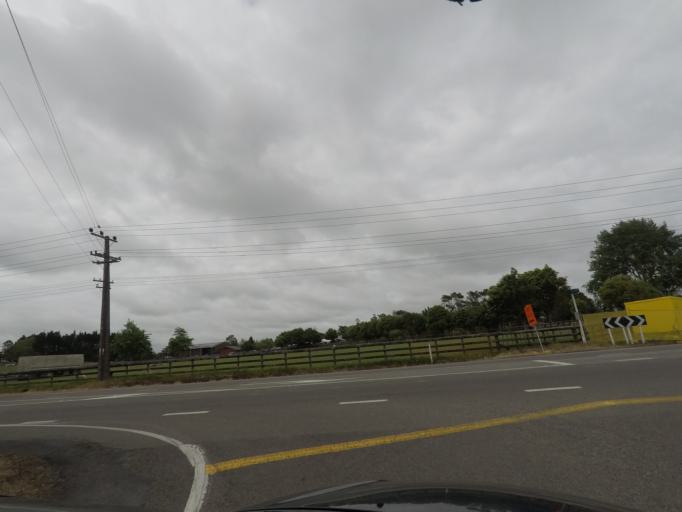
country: NZ
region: Auckland
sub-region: Auckland
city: Muriwai Beach
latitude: -36.7786
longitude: 174.5663
